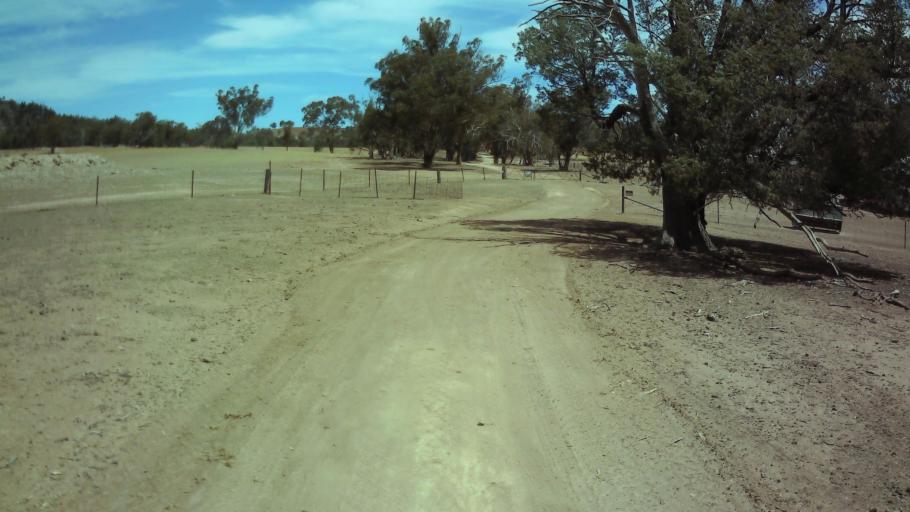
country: AU
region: New South Wales
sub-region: Weddin
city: Grenfell
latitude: -33.7775
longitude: 148.1515
